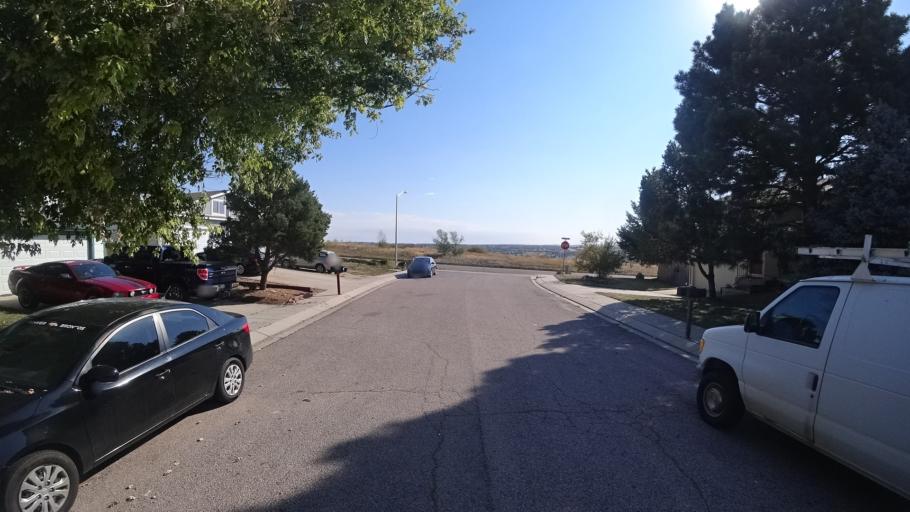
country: US
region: Colorado
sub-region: El Paso County
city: Cimarron Hills
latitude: 38.8887
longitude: -104.7234
